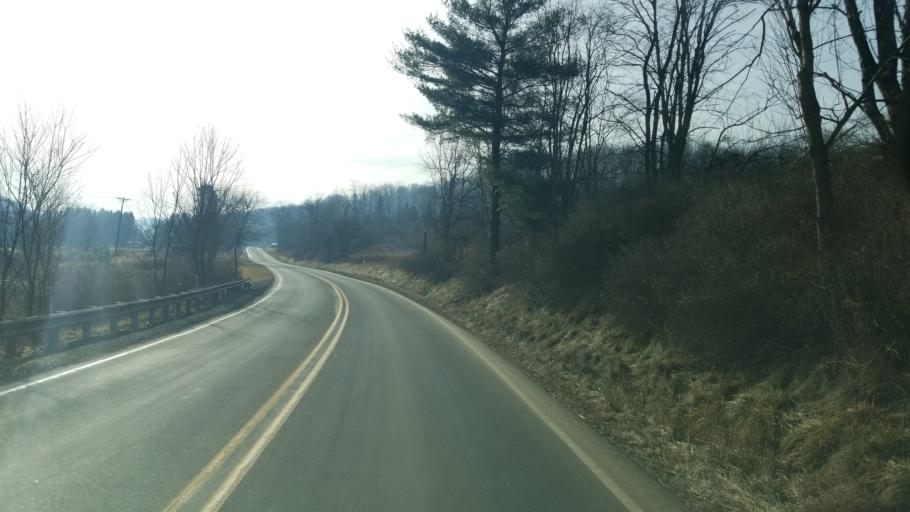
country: US
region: Pennsylvania
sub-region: Indiana County
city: Chevy Chase Heights
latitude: 40.7788
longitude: -79.1548
